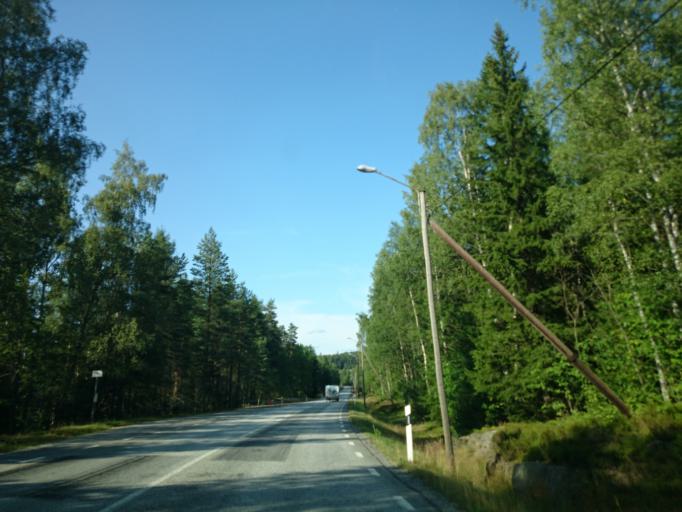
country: SE
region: Vaestmanland
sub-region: Skinnskattebergs Kommun
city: Skinnskatteberg
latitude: 59.8147
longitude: 15.5283
